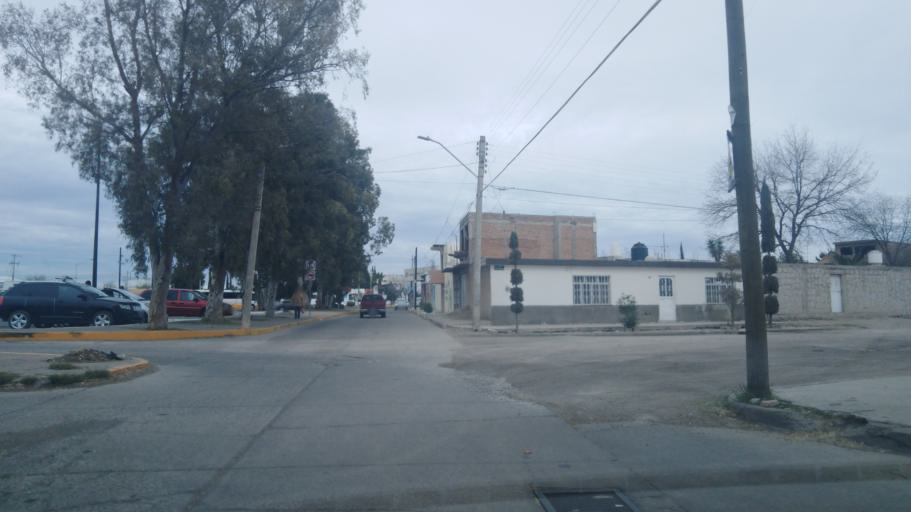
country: MX
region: Durango
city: Victoria de Durango
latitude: 24.0309
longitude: -104.6279
